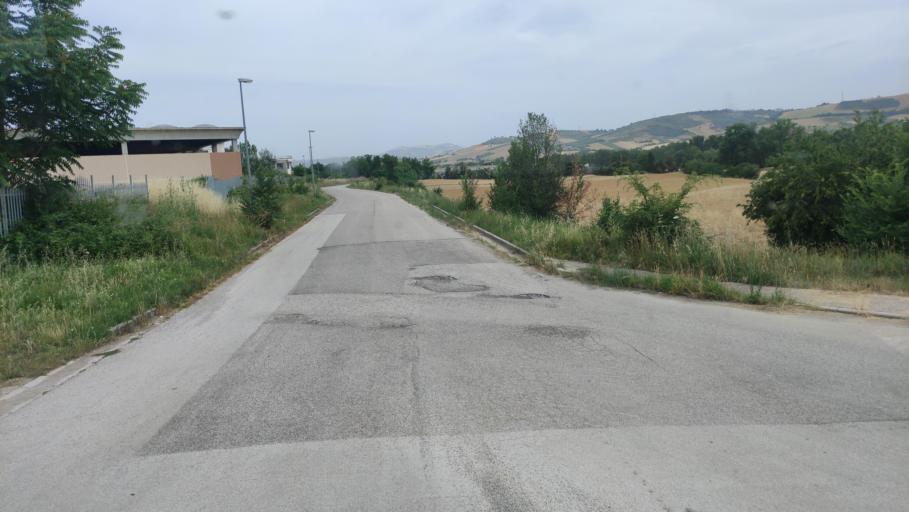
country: IT
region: Campania
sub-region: Provincia di Avellino
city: Sturno
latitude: 41.0468
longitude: 15.1304
